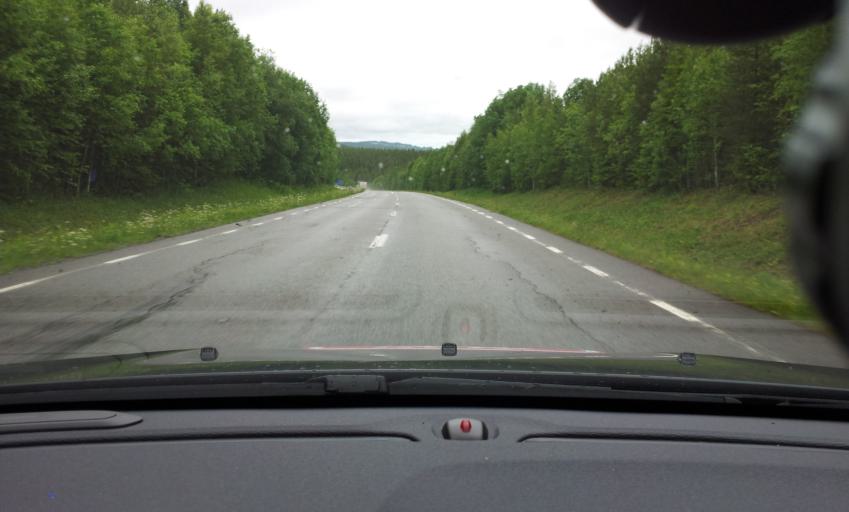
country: SE
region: Jaemtland
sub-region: OEstersunds Kommun
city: Lit
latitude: 63.6083
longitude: 14.6729
